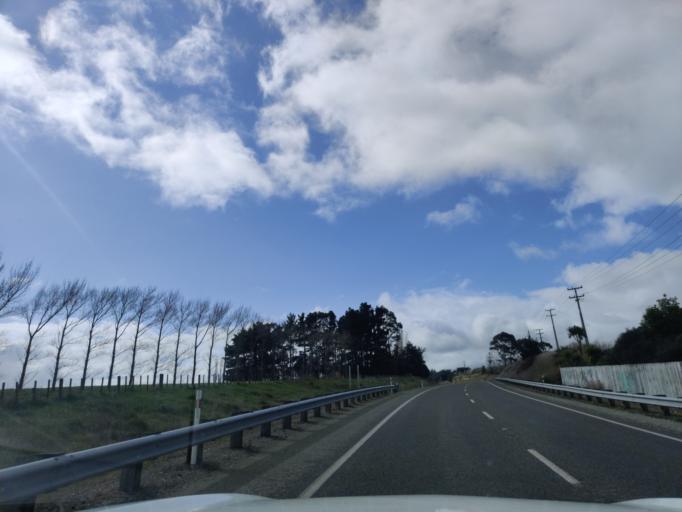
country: NZ
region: Manawatu-Wanganui
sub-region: Palmerston North City
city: Palmerston North
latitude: -40.4060
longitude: 175.6117
